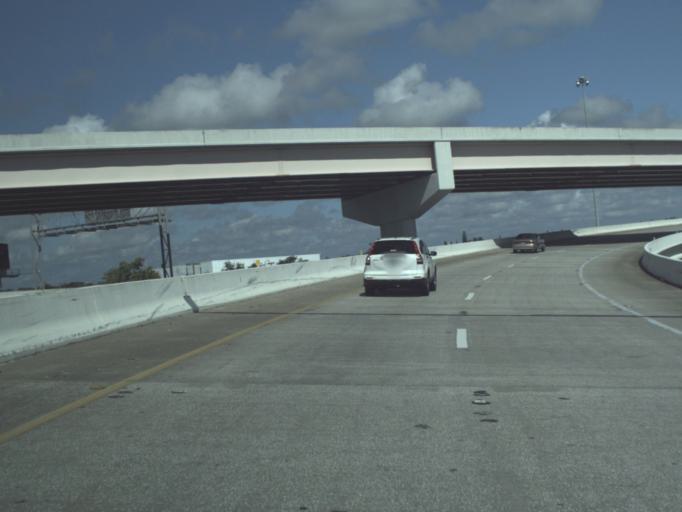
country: US
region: Florida
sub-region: Pinellas County
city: Saint Petersburg
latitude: 27.7668
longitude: -82.6572
